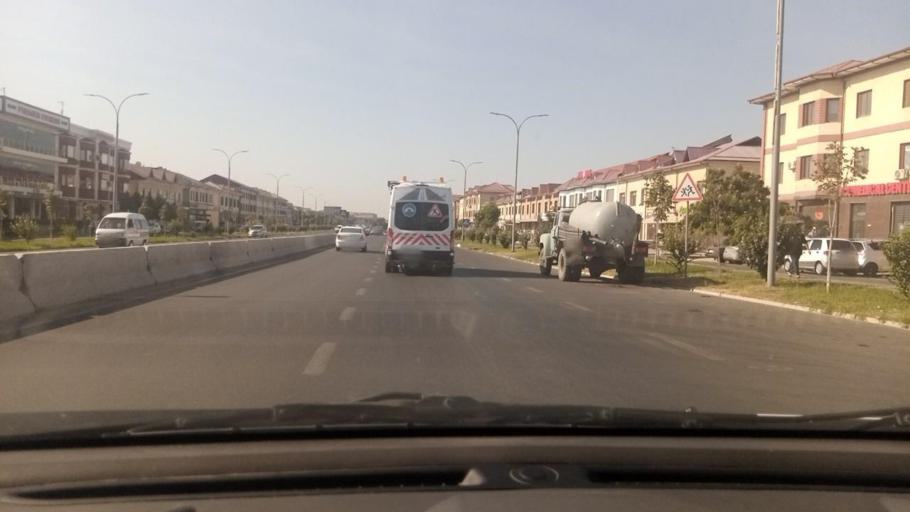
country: UZ
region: Toshkent Shahri
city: Bektemir
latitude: 41.2230
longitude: 69.3339
